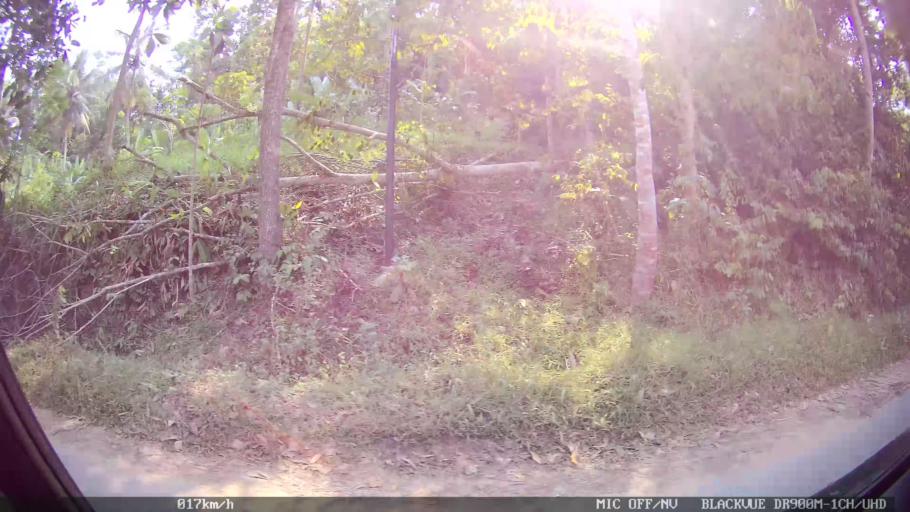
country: ID
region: Lampung
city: Pringsewu
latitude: -5.3873
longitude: 104.9937
